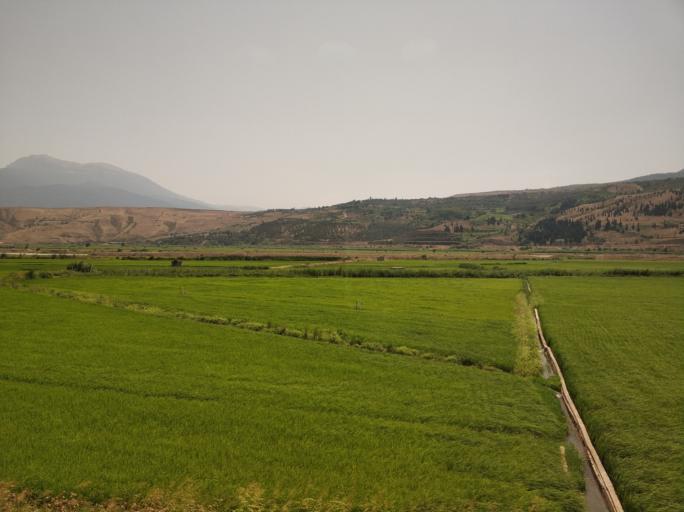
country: IR
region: Gilan
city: Pa'in-e Bazar-e Rudbar
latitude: 36.8753
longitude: 49.4943
